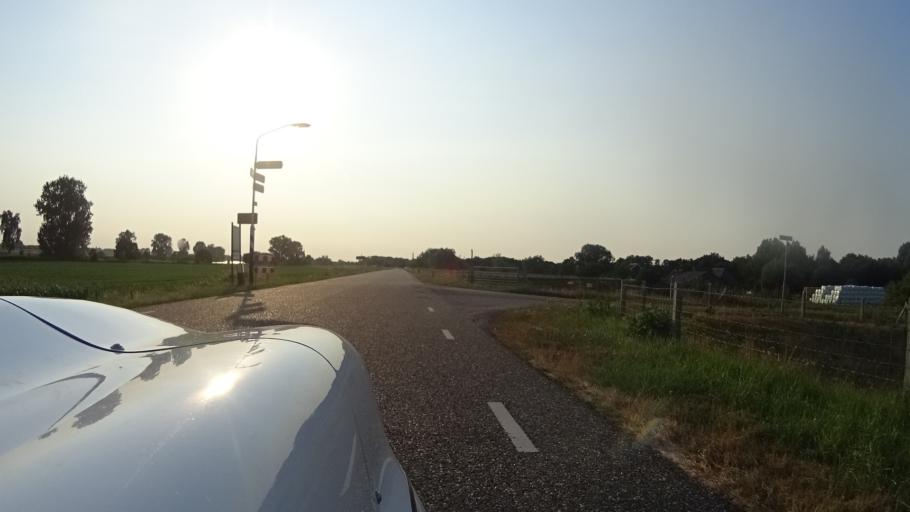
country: NL
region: Gelderland
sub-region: Gemeente Druten
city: Druten
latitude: 51.8274
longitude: 5.6069
